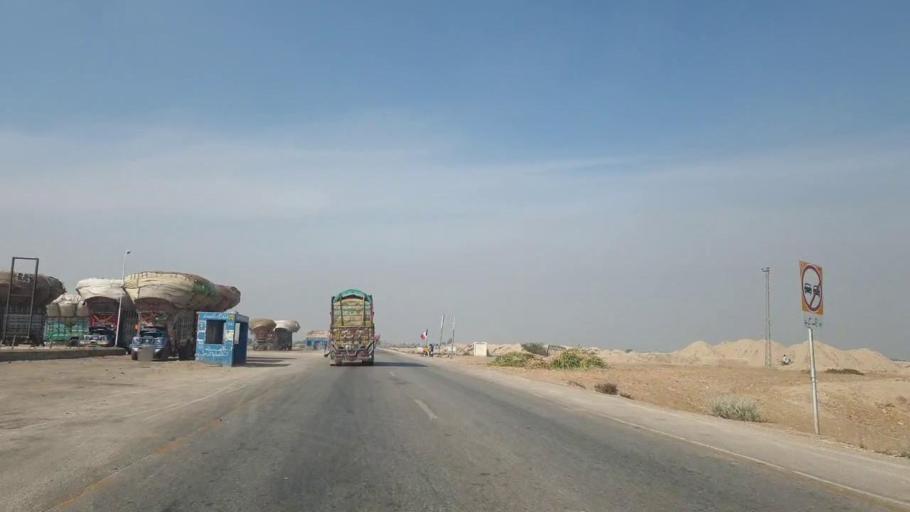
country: PK
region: Sindh
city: Sann
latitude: 25.9519
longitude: 68.1965
